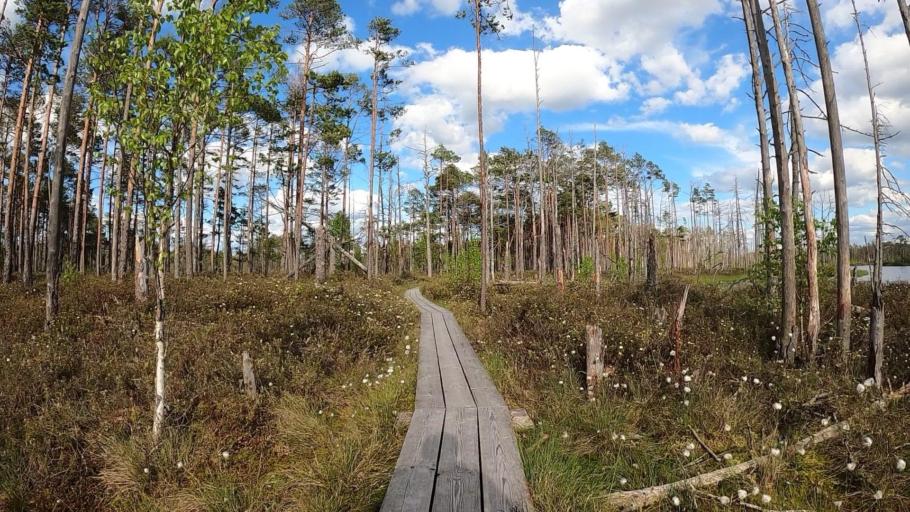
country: LV
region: Jurmala
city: Jurmala
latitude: 56.8512
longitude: 23.8159
